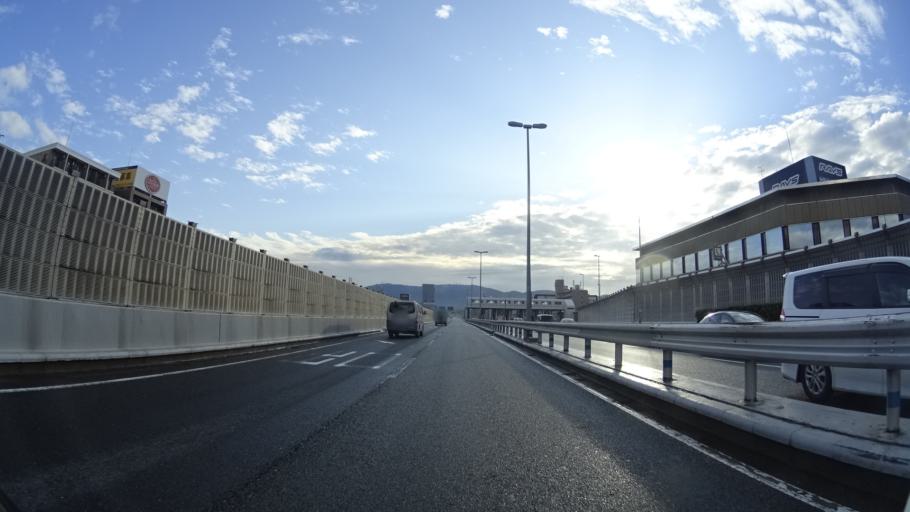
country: JP
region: Osaka
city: Daitocho
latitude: 34.6788
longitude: 135.5847
